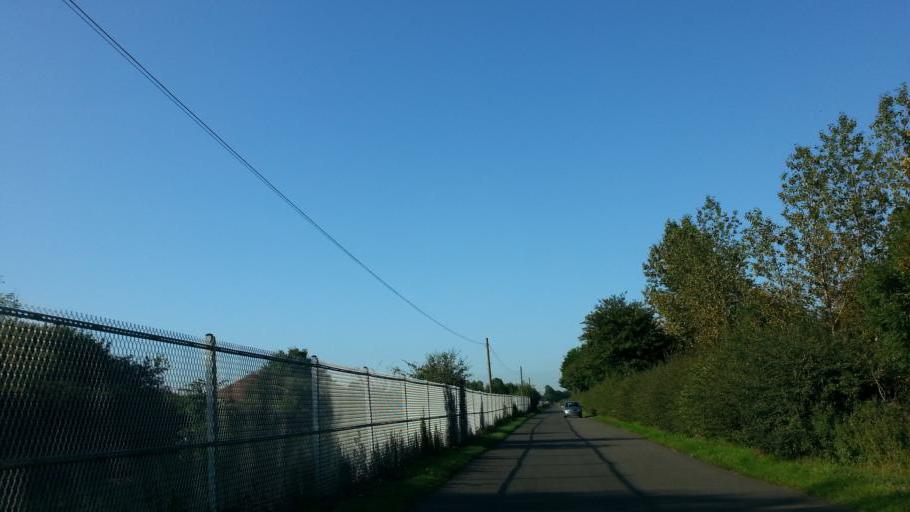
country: GB
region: England
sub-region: Leicestershire
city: Queniborough
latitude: 52.7177
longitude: -1.0582
